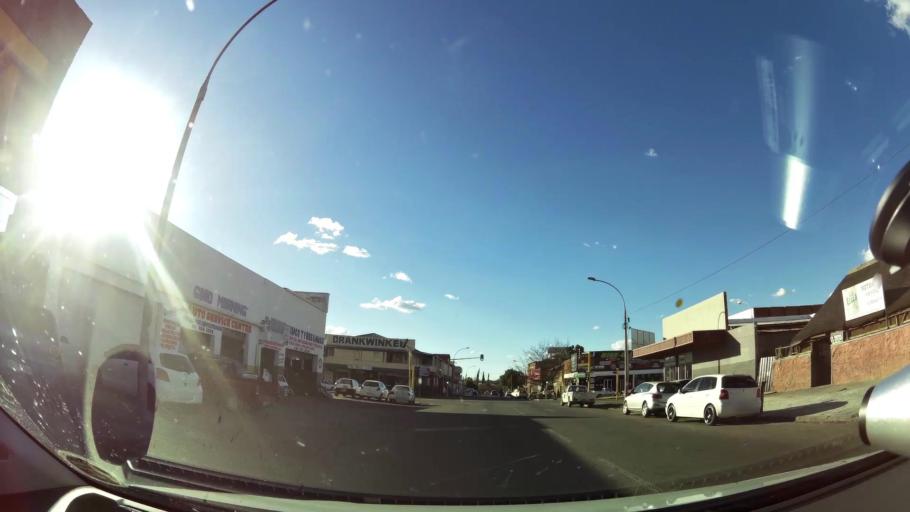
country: ZA
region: North-West
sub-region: Dr Kenneth Kaunda District Municipality
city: Klerksdorp
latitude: -26.8660
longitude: 26.6679
